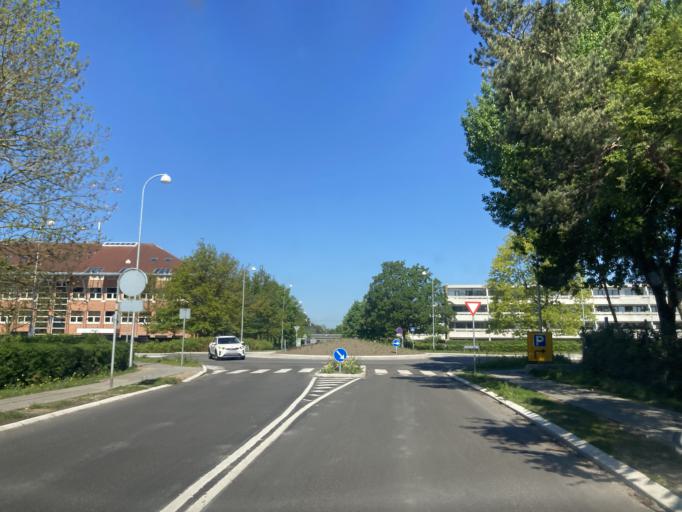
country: DK
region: Capital Region
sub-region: Ishoj Kommune
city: Ishoj
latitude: 55.6164
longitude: 12.3652
